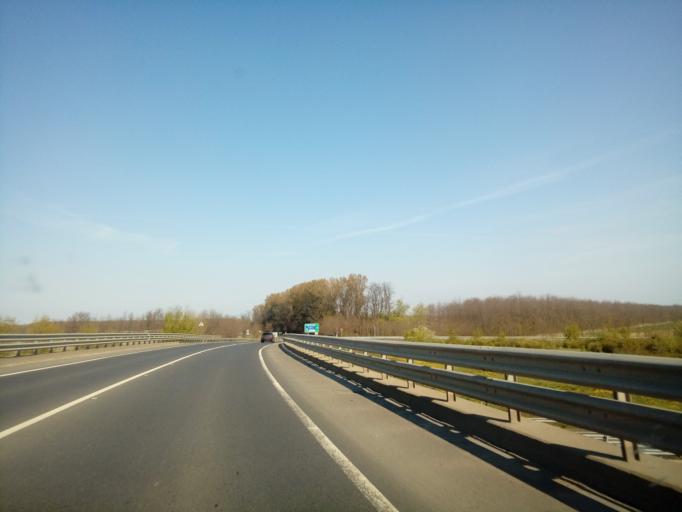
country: HU
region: Szabolcs-Szatmar-Bereg
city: Nagykallo
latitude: 47.8928
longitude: 21.8038
